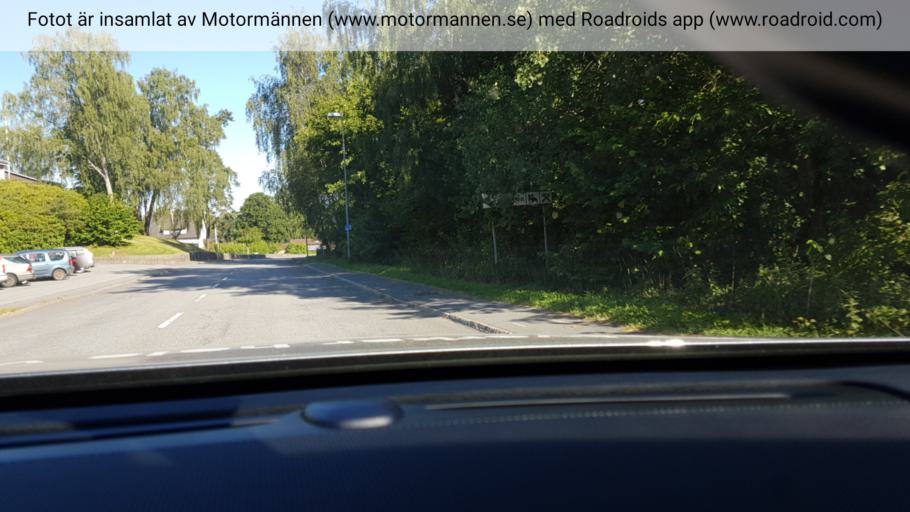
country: SE
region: Skane
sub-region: Hassleholms Kommun
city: Bjarnum
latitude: 56.3349
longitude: 13.6703
